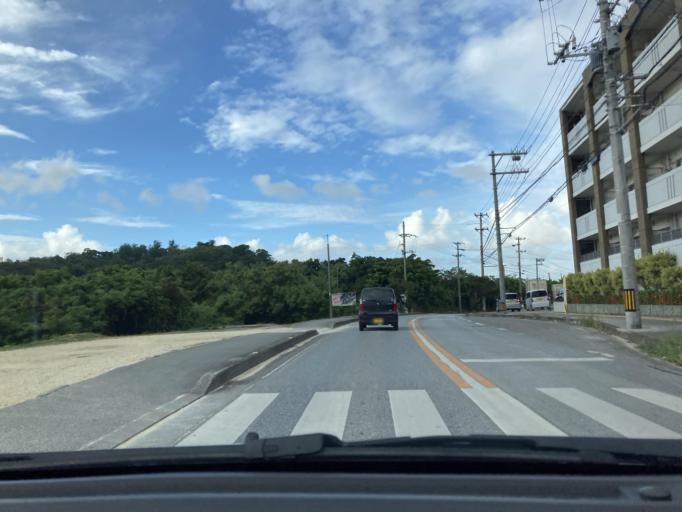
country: JP
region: Okinawa
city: Tomigusuku
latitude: 26.1821
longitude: 127.6852
